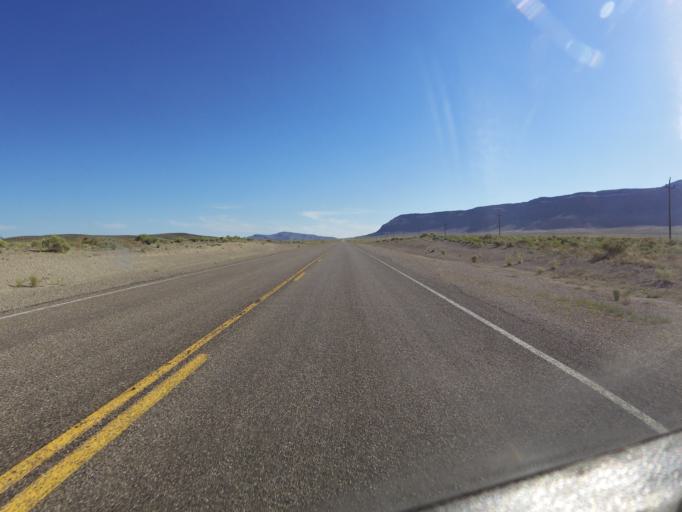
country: US
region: Nevada
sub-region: Nye County
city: Tonopah
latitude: 38.3745
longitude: -116.2249
